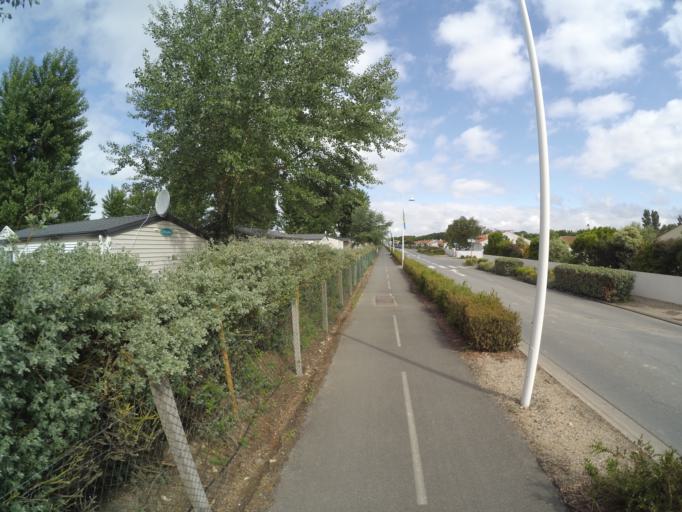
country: FR
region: Poitou-Charentes
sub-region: Departement de la Charente-Maritime
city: Chatelaillon-Plage
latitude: 46.0854
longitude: -1.0941
